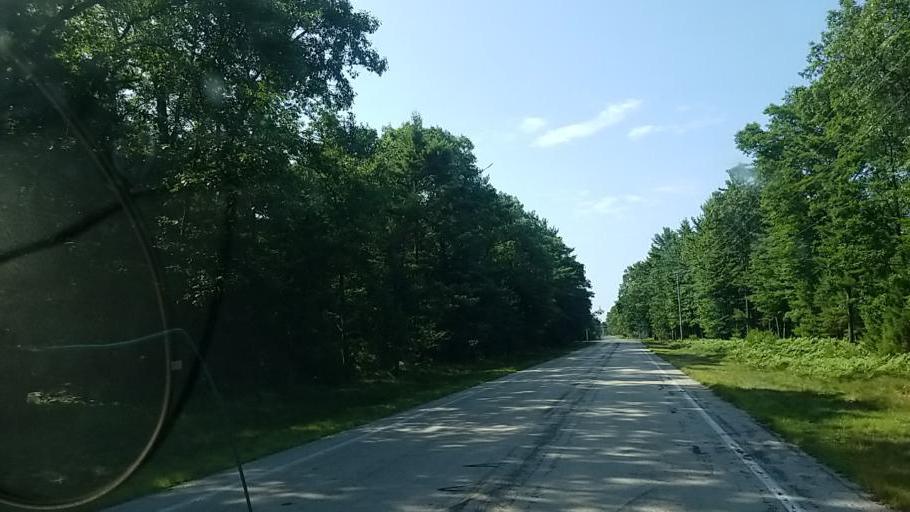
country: US
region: Michigan
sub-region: Muskegon County
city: Whitehall
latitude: 43.3147
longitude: -86.3771
